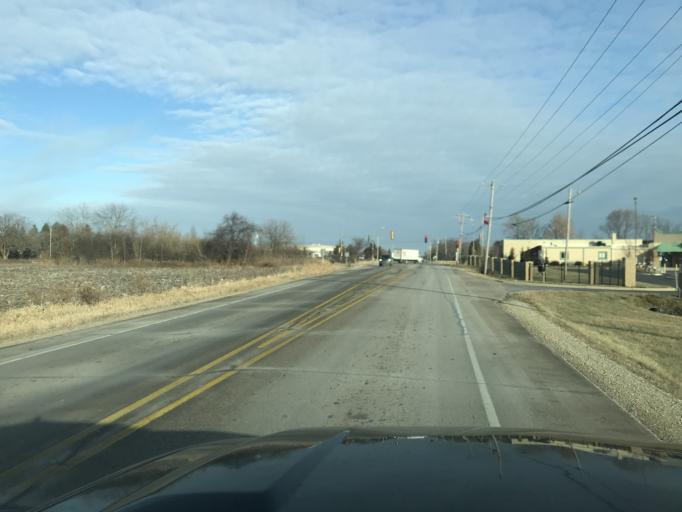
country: US
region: Wisconsin
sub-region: Kenosha County
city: Pleasant Prairie
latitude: 42.5808
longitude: -87.9146
